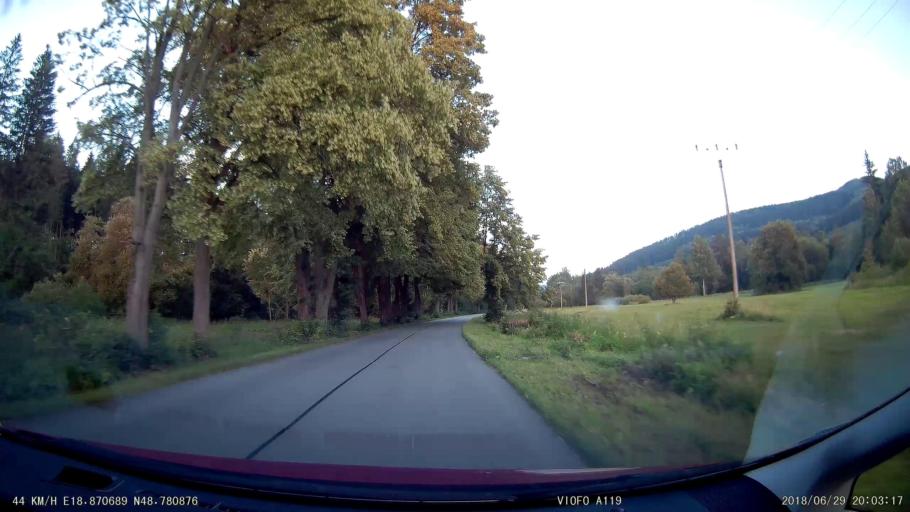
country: SK
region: Banskobystricky
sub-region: Okres Ziar nad Hronom
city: Kremnica
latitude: 48.7808
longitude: 18.8709
